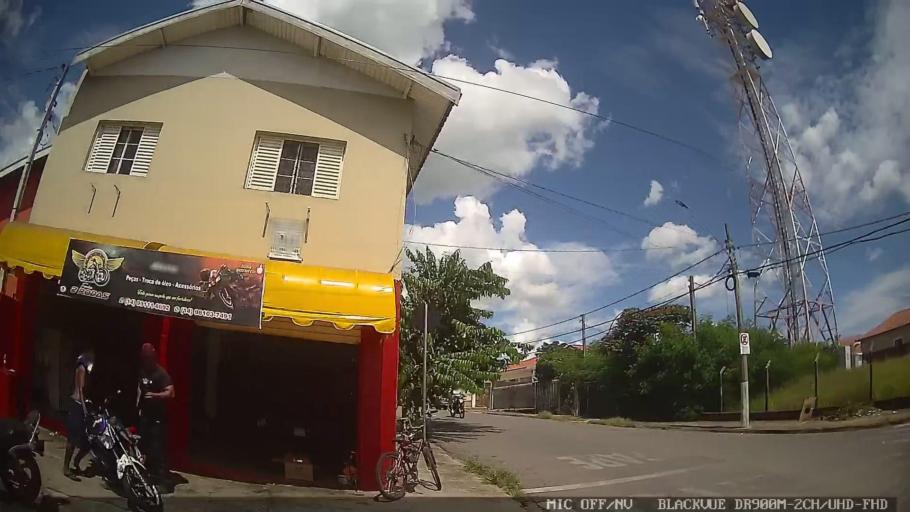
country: BR
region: Sao Paulo
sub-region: Conchas
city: Conchas
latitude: -23.0220
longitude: -48.0114
